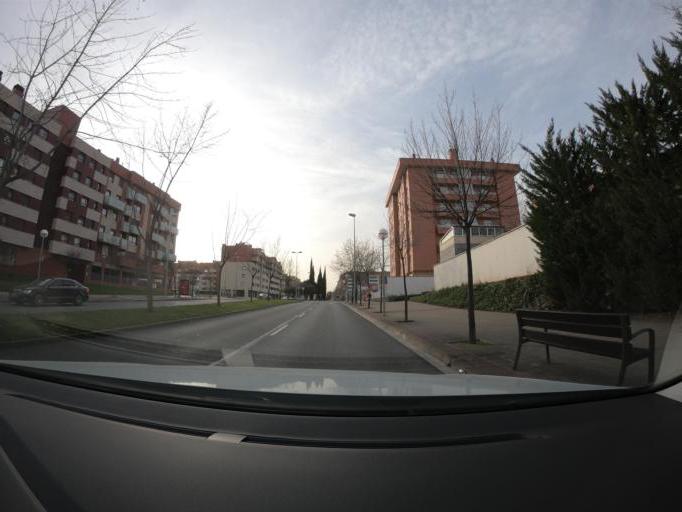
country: ES
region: La Rioja
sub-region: Provincia de La Rioja
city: Logrono
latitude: 42.4530
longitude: -2.4586
